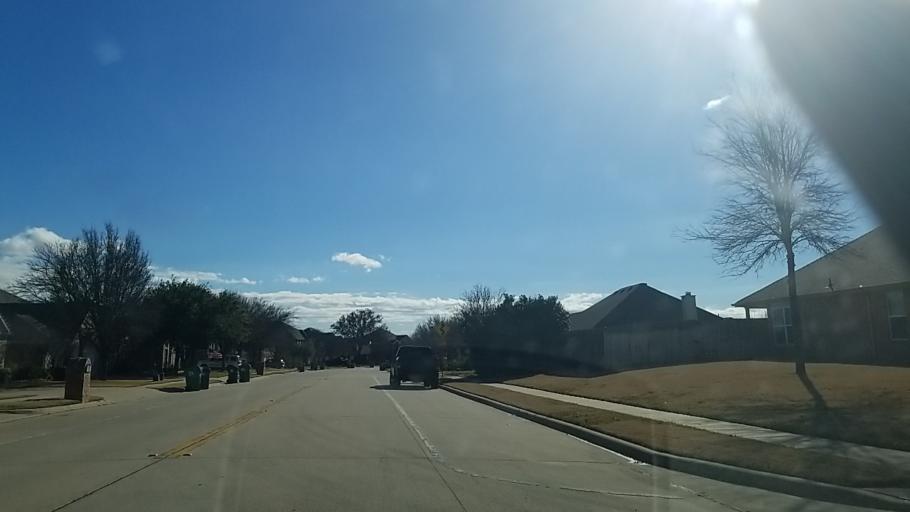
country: US
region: Texas
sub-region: Denton County
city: Corinth
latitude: 33.1538
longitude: -97.0911
